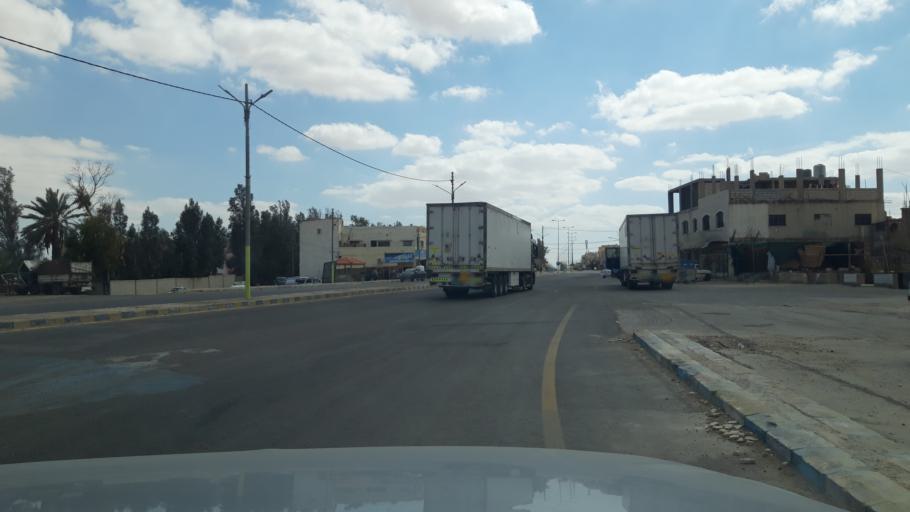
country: JO
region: Amman
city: Al Azraq ash Shamali
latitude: 31.8367
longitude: 36.8153
